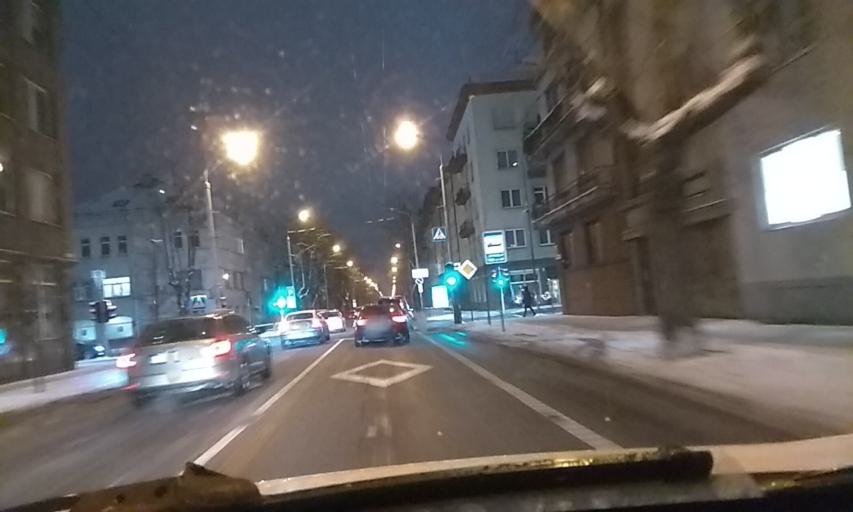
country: LT
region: Kauno apskritis
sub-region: Kaunas
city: Kaunas
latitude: 54.8955
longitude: 23.9181
